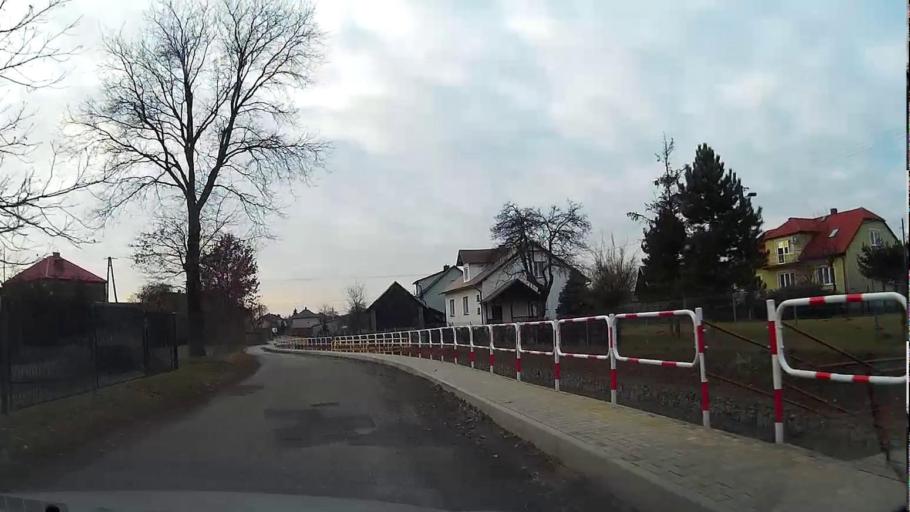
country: PL
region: Lesser Poland Voivodeship
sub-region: Powiat chrzanowski
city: Kwaczala
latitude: 50.0632
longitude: 19.4880
